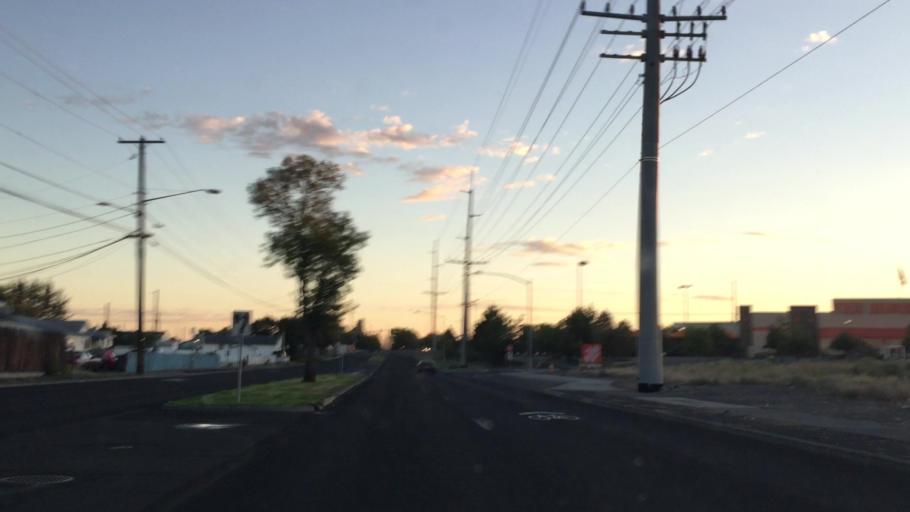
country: US
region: Washington
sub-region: Grant County
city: Moses Lake
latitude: 47.1465
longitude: -119.2942
